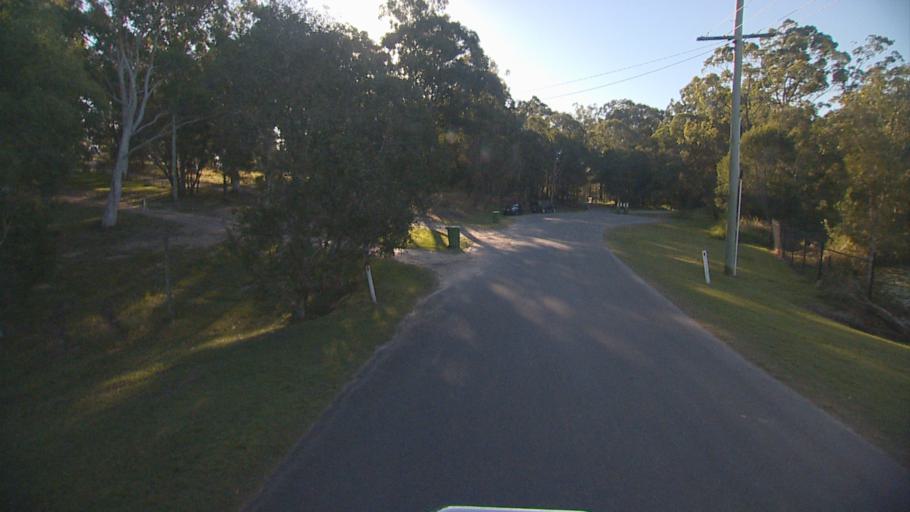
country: AU
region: Queensland
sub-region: Redland
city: Redland Bay
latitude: -27.6583
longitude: 153.2747
